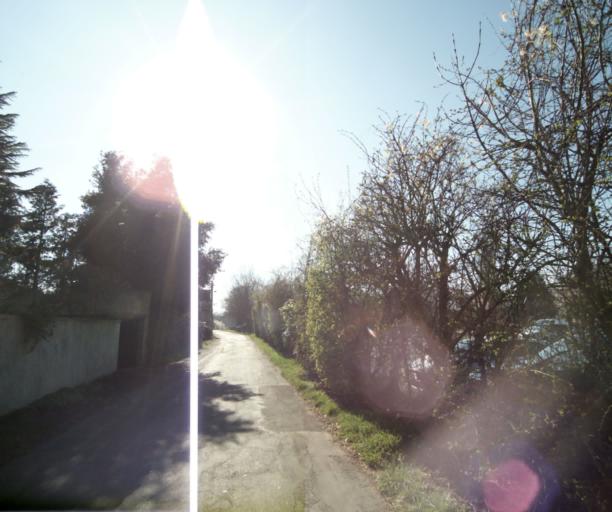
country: FR
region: Ile-de-France
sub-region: Departement du Val-d'Oise
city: Neuville-sur-Oise
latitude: 49.0286
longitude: 2.0568
